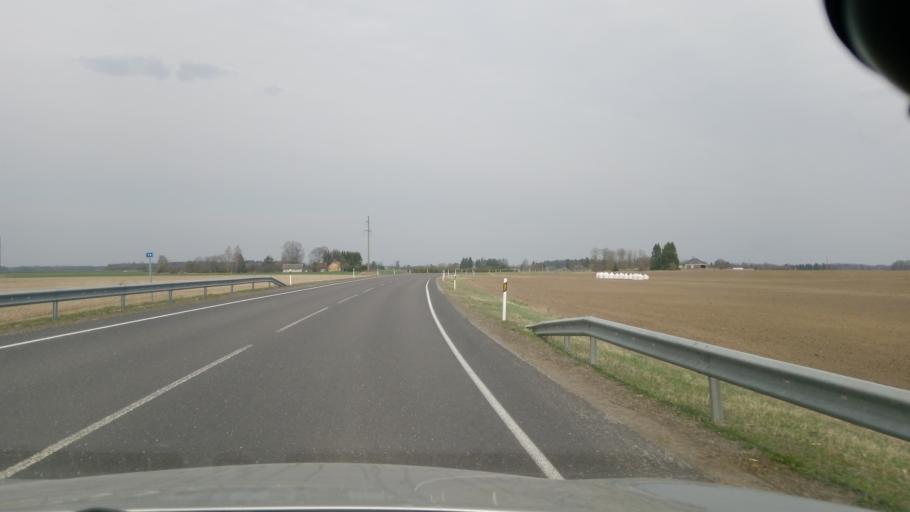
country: EE
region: Viljandimaa
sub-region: Vohma linn
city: Vohma
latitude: 58.6781
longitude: 25.6061
